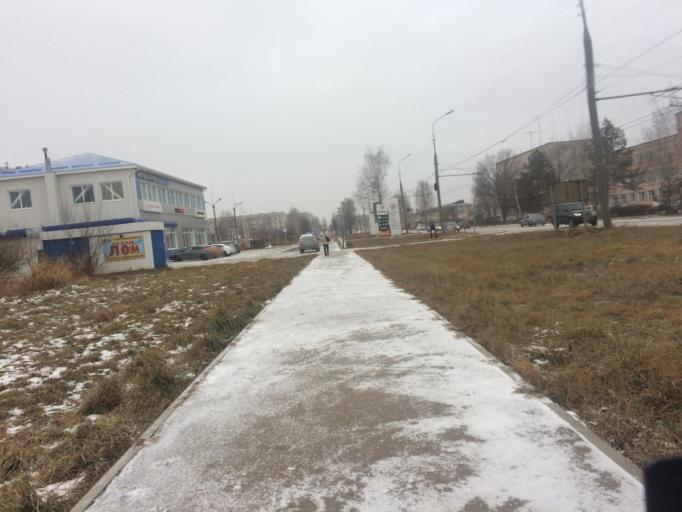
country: RU
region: Mariy-El
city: Yoshkar-Ola
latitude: 56.6541
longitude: 47.8740
